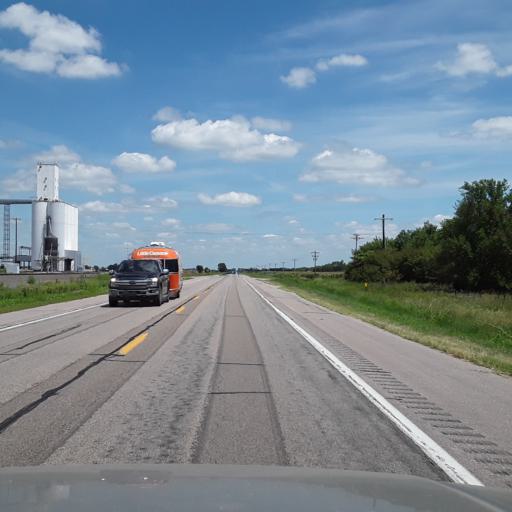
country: US
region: Nebraska
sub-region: Nance County
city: Genoa
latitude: 41.3262
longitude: -97.6391
